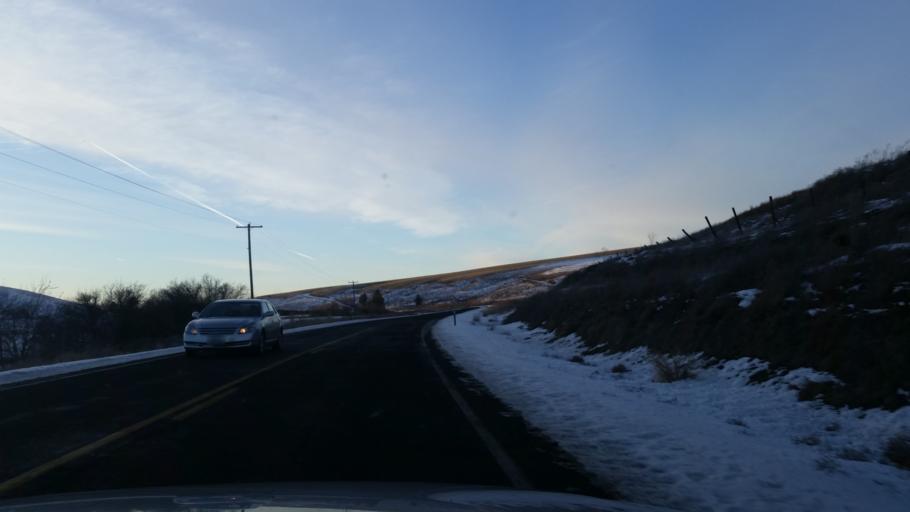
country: US
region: Washington
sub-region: Spokane County
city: Cheney
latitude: 47.1170
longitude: -117.6766
